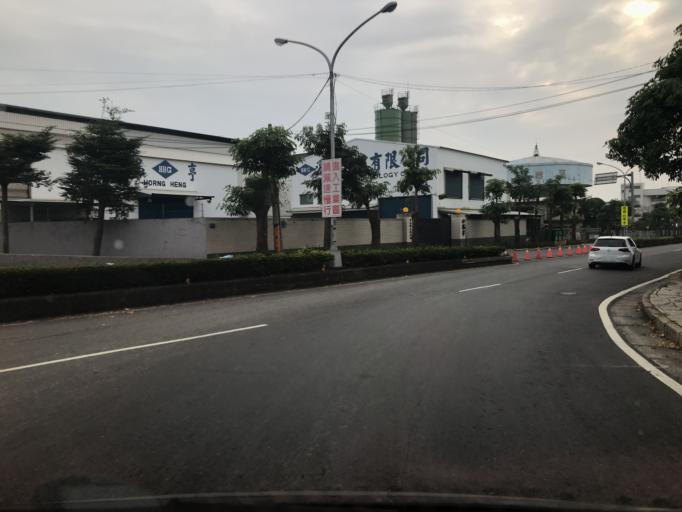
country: TW
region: Taiwan
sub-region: Pingtung
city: Pingtung
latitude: 22.4144
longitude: 120.5850
